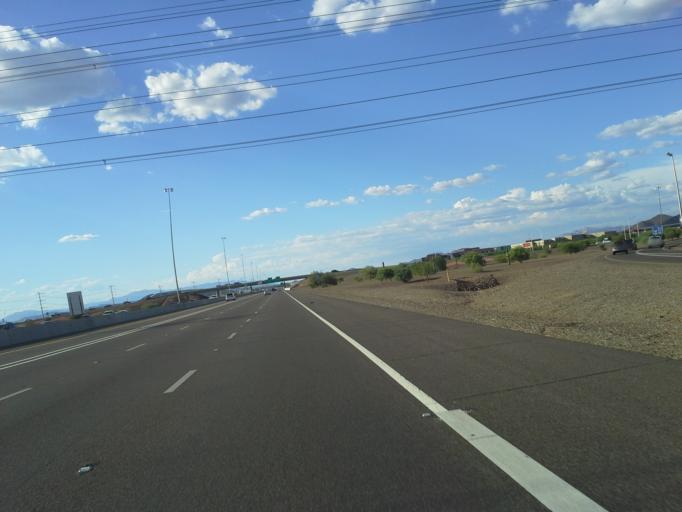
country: US
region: Arizona
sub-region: Maricopa County
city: Anthem
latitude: 33.7091
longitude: -112.1165
